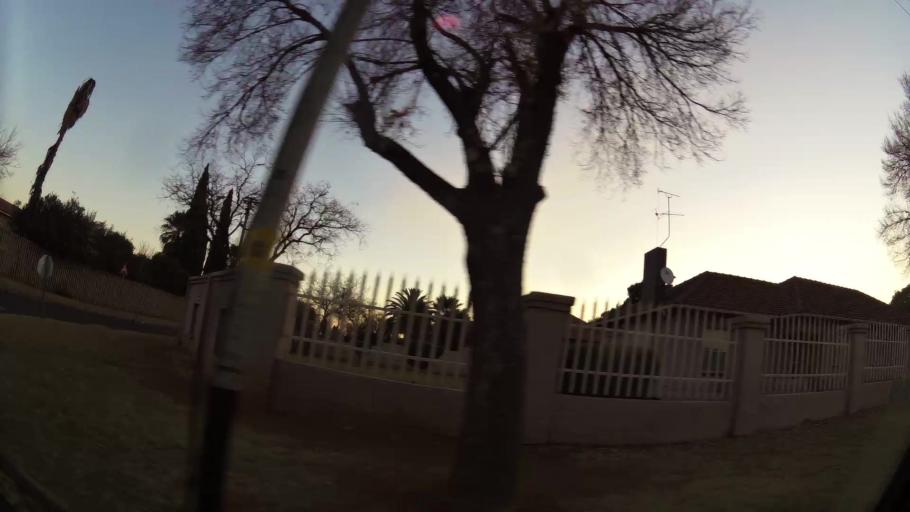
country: ZA
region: Gauteng
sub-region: Ekurhuleni Metropolitan Municipality
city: Germiston
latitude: -26.2655
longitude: 28.1630
